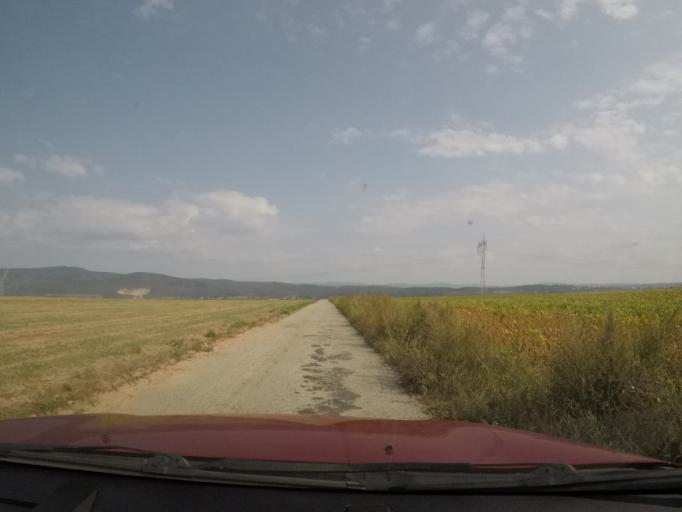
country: SK
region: Kosicky
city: Moldava nad Bodvou
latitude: 48.5850
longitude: 20.9566
